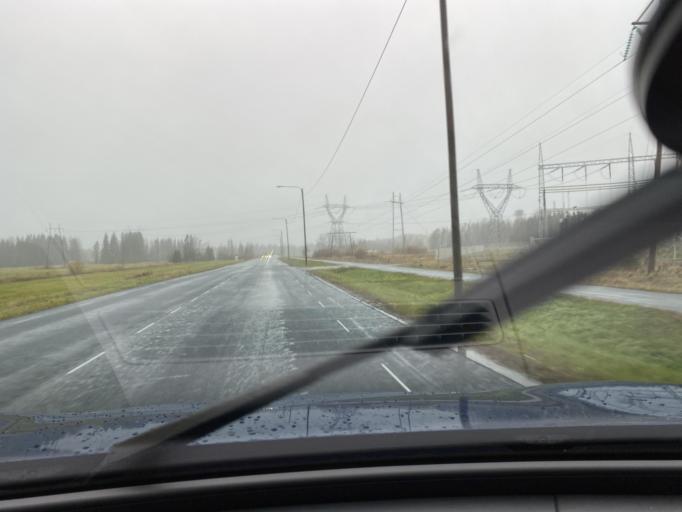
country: FI
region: Haeme
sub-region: Forssa
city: Forssa
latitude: 60.8009
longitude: 23.5741
